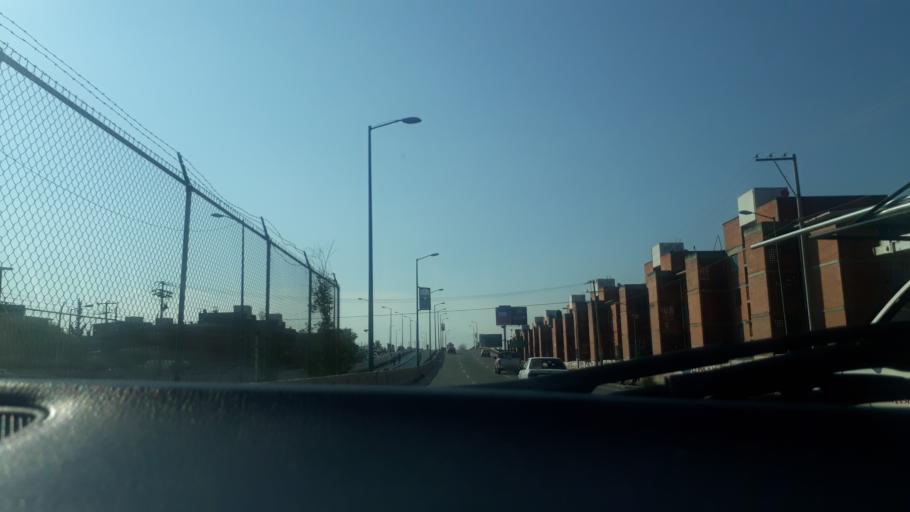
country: MX
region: Puebla
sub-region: Puebla
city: El Capulo (La Quebradora)
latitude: 18.9908
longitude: -98.2426
